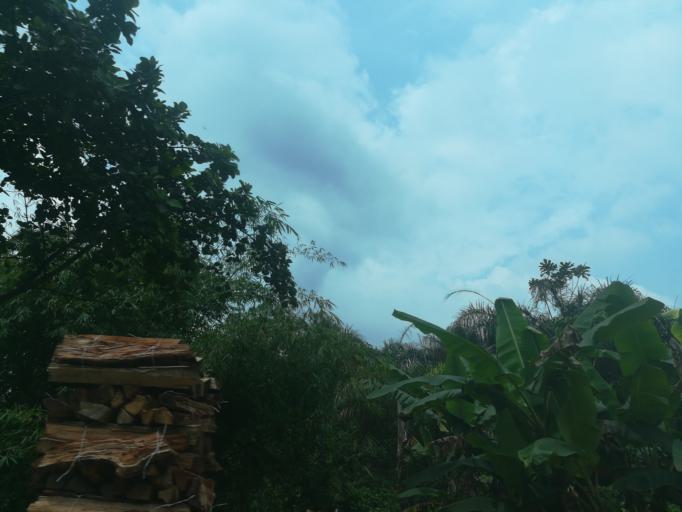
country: NG
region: Lagos
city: Ikorodu
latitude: 6.6743
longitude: 3.6517
